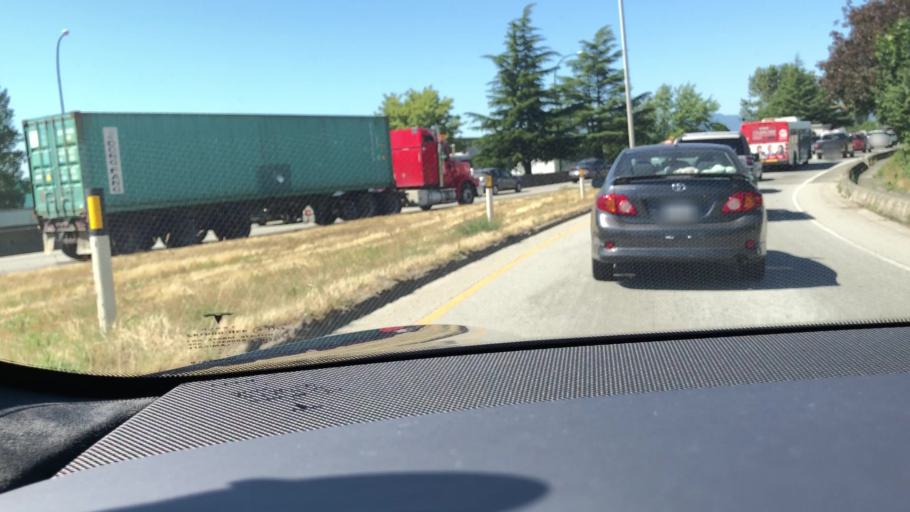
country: CA
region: British Columbia
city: Richmond
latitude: 49.1940
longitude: -123.0795
